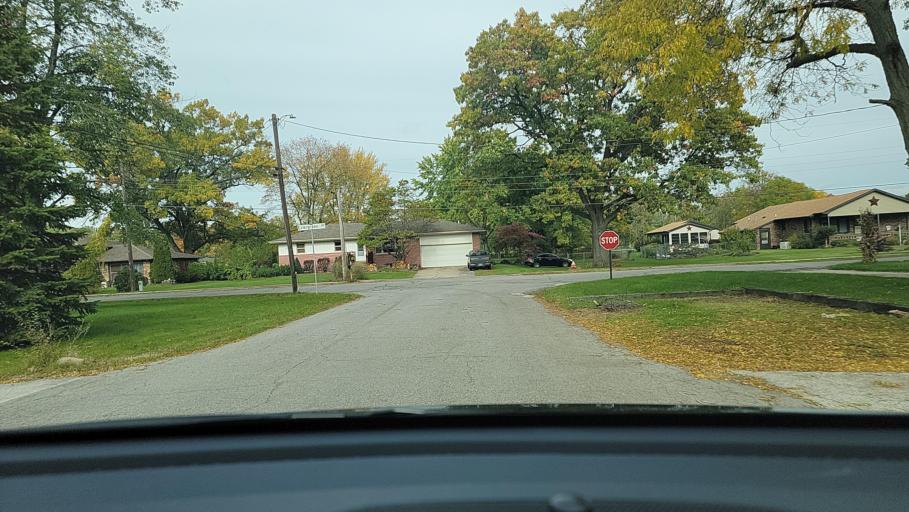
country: US
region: Indiana
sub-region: Porter County
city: Portage
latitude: 41.5792
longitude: -87.1916
